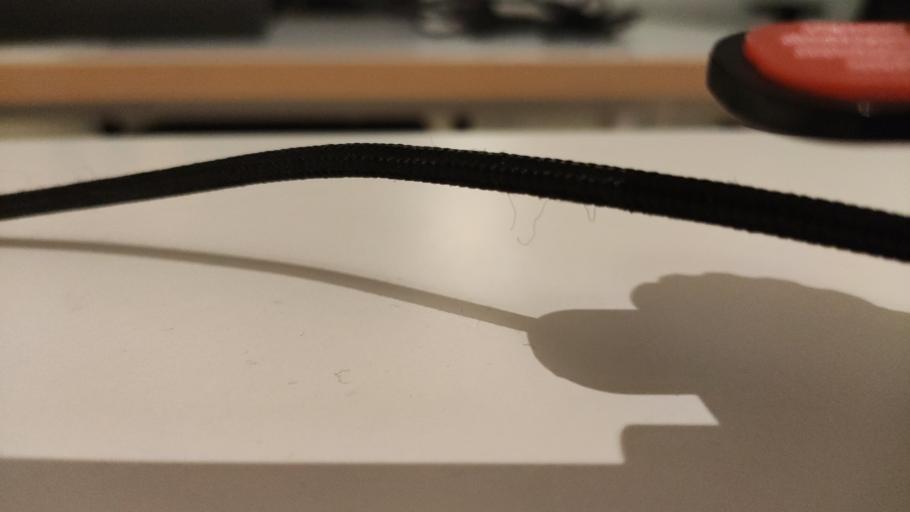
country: RU
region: Moskovskaya
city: Kurovskoye
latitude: 55.5792
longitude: 38.8888
